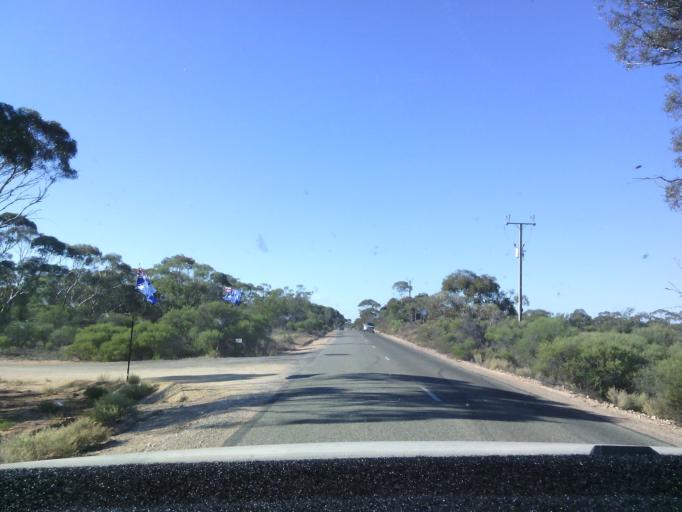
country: AU
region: South Australia
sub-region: Berri and Barmera
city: Monash
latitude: -34.2430
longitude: 140.5924
